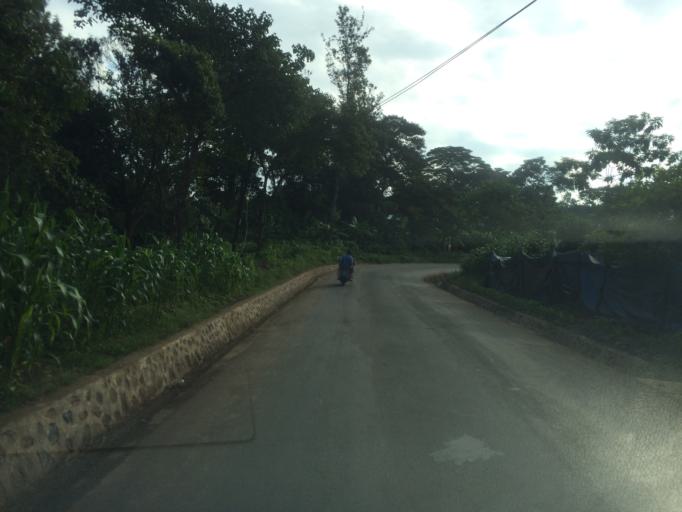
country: TZ
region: Arusha
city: Usa River
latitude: -3.3717
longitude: 36.8182
